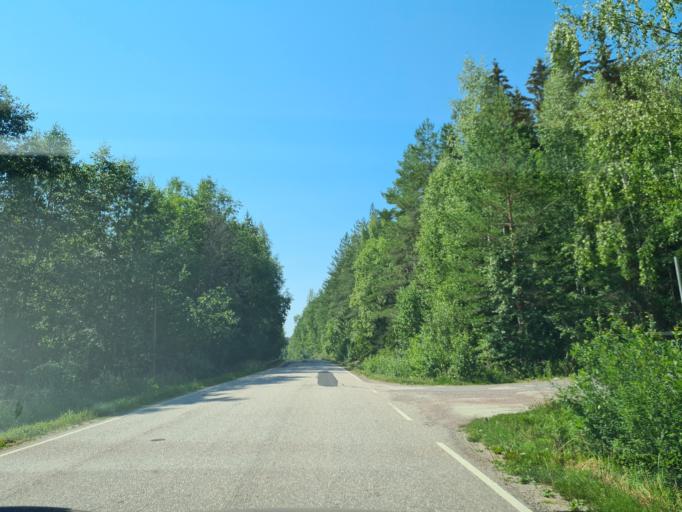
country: FI
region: Varsinais-Suomi
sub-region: Loimaa
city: Aura
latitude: 60.6036
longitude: 22.5842
